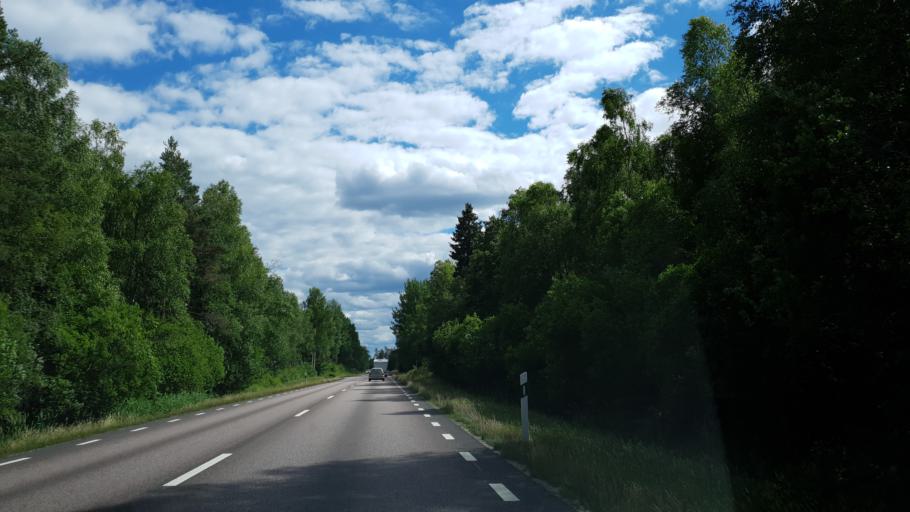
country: SE
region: Kronoberg
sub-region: Lessebo Kommun
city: Lessebo
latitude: 56.8410
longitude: 15.3908
